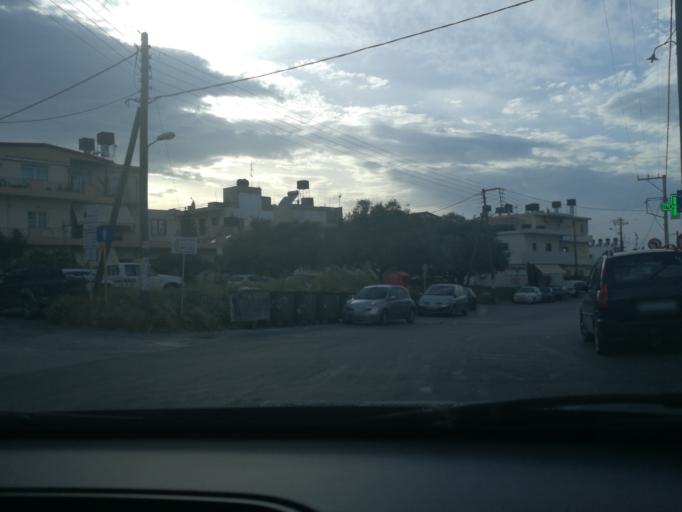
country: GR
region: Crete
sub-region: Nomos Irakleiou
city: Irakleion
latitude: 35.3174
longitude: 25.1360
